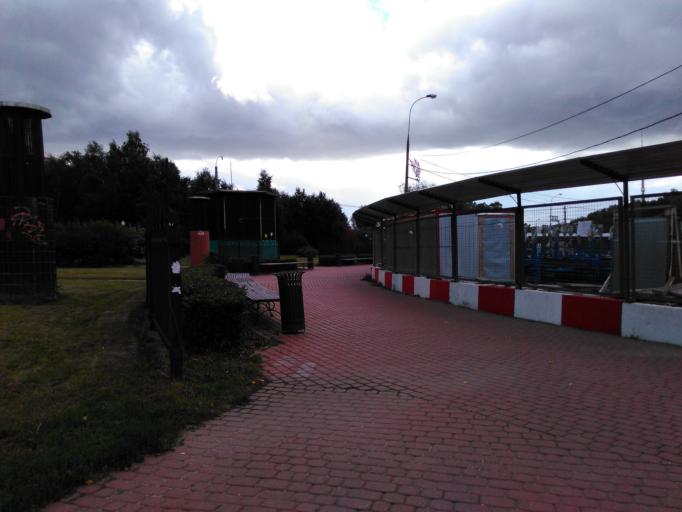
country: RU
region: Moscow
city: Sviblovo
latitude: 55.8441
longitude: 37.6383
